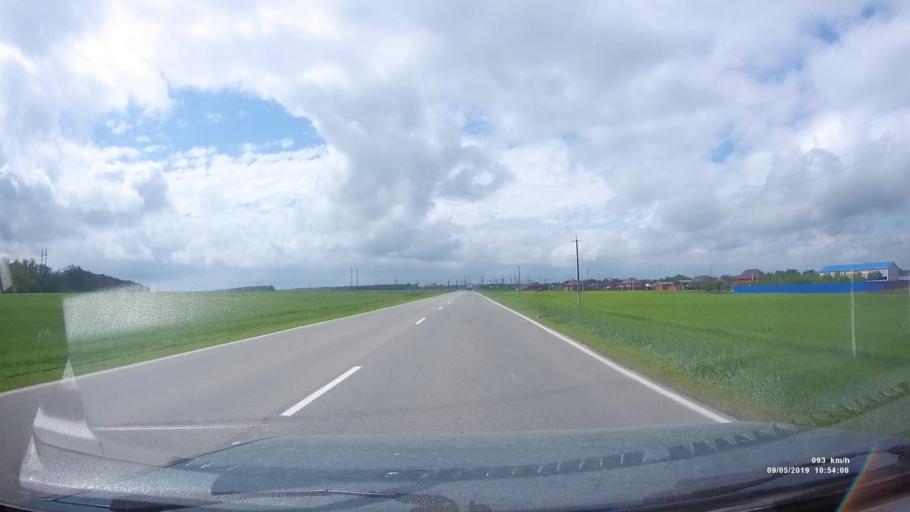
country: RU
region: Rostov
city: Peshkovo
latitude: 46.8814
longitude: 39.3345
